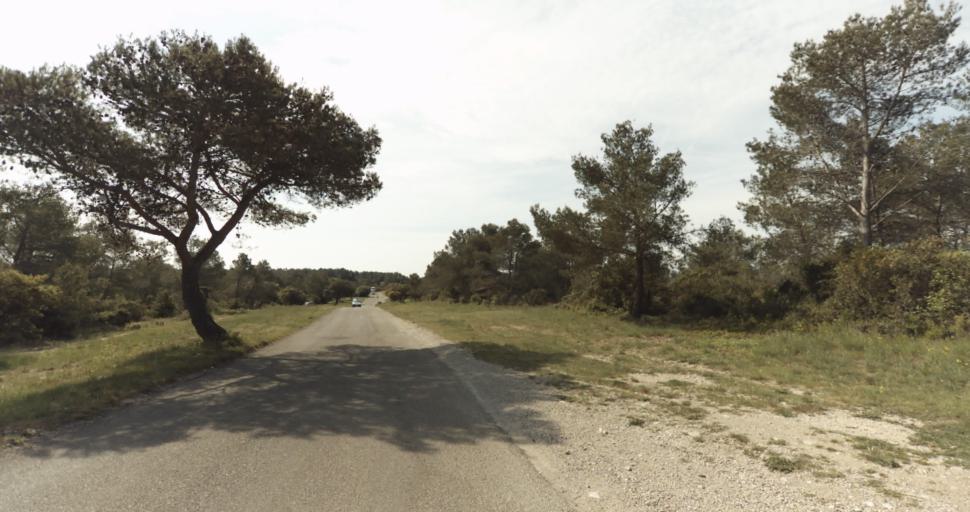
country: FR
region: Languedoc-Roussillon
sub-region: Departement du Gard
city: Poulx
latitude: 43.8777
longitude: 4.3907
